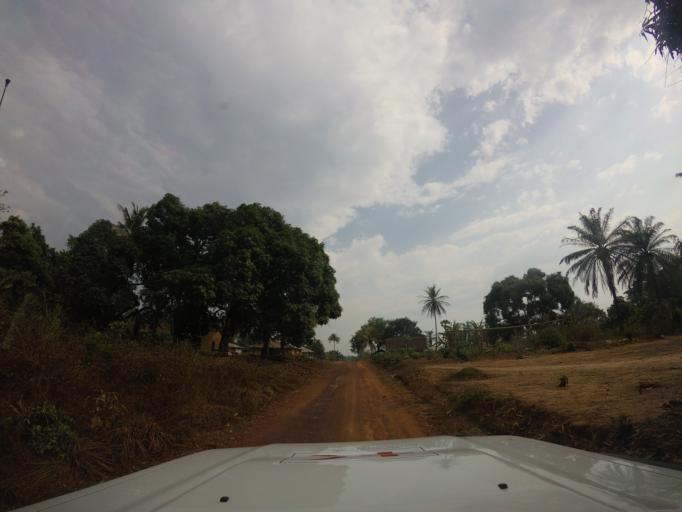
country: LR
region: Grand Cape Mount
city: Robertsport
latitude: 7.0243
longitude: -11.2892
